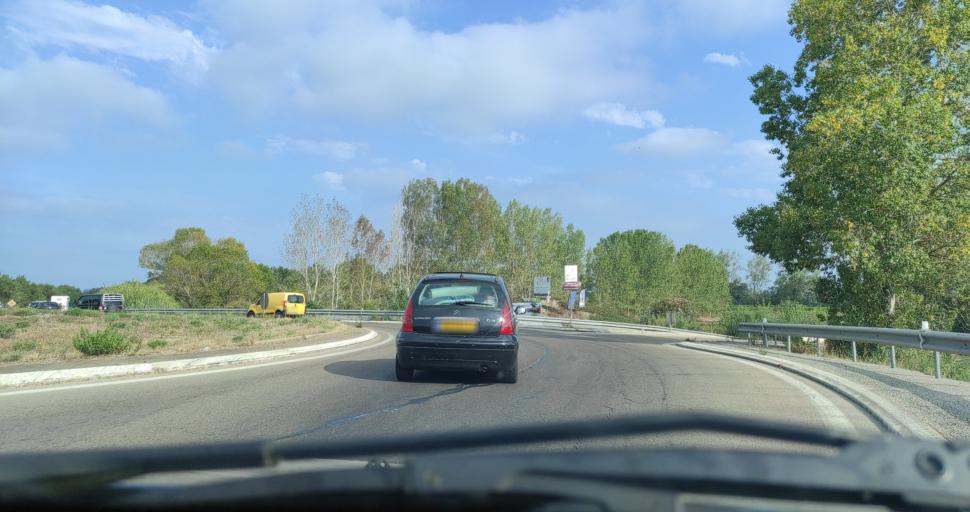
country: FR
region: Languedoc-Roussillon
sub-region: Departement du Gard
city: Le Grau-du-Roi
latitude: 43.5659
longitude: 4.1244
